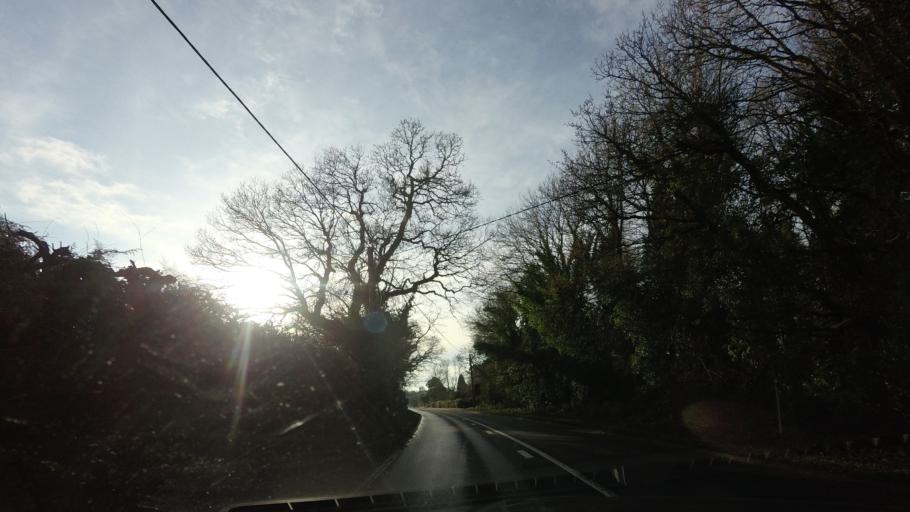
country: GB
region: England
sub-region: East Sussex
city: Battle
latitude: 50.8996
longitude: 0.4514
